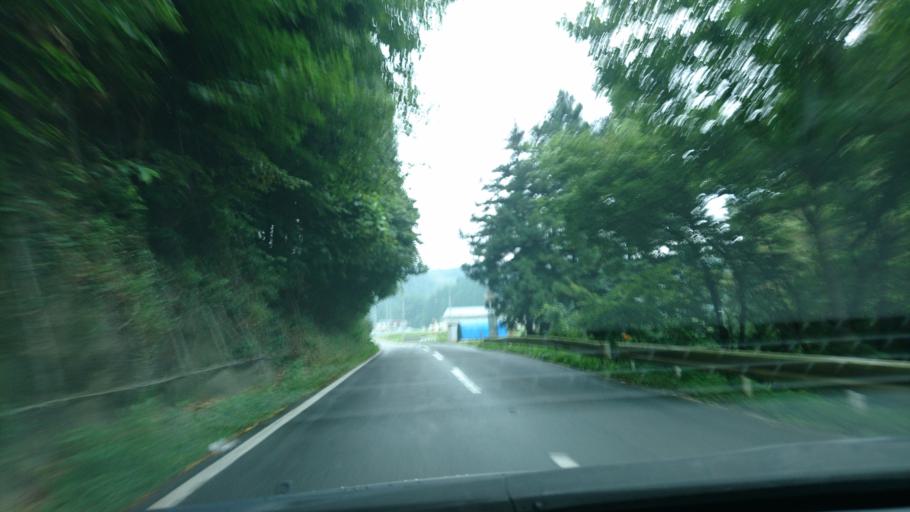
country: JP
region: Iwate
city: Ichinoseki
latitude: 39.0068
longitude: 141.2605
